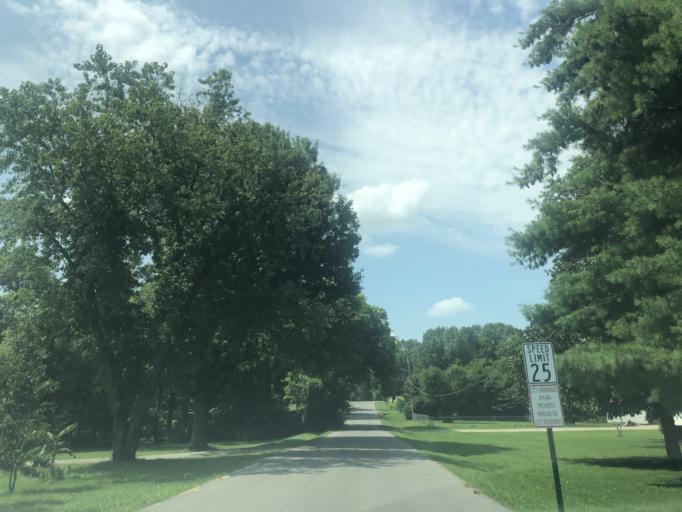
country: US
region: Tennessee
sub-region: Rutherford County
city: La Vergne
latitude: 36.0154
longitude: -86.5873
